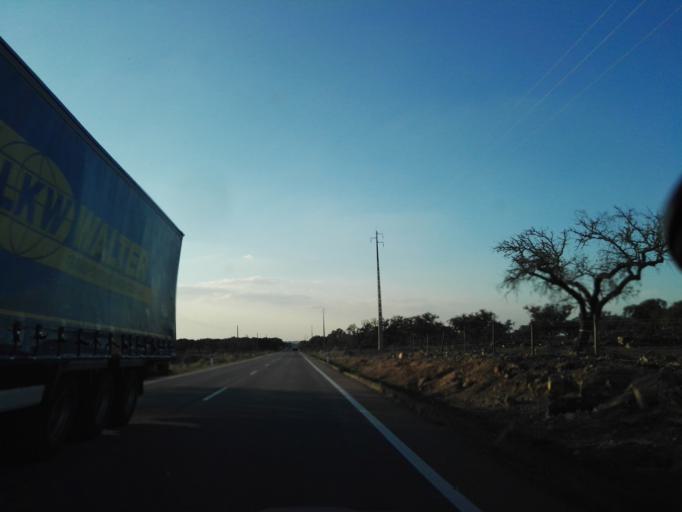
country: PT
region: Evora
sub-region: Arraiolos
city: Arraiolos
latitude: 38.8610
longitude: -7.9288
